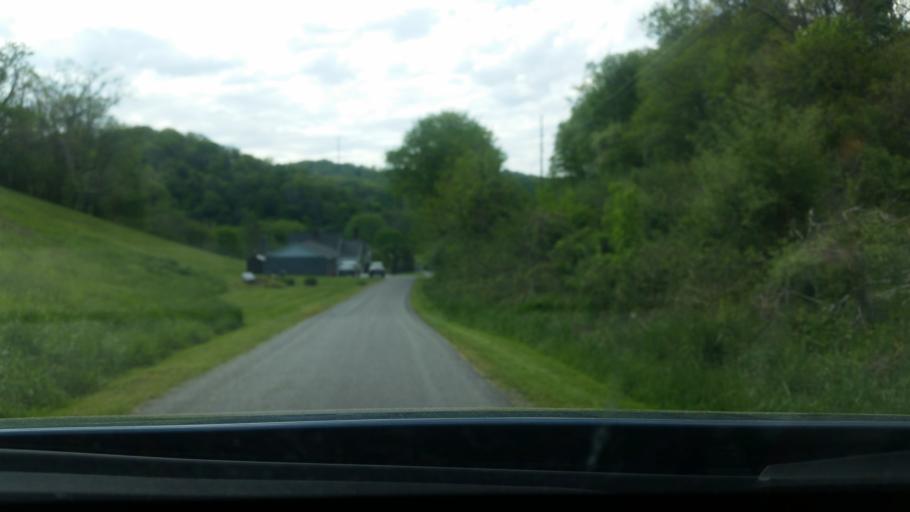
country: US
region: Virginia
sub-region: Giles County
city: Pembroke
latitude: 37.3163
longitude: -80.6315
